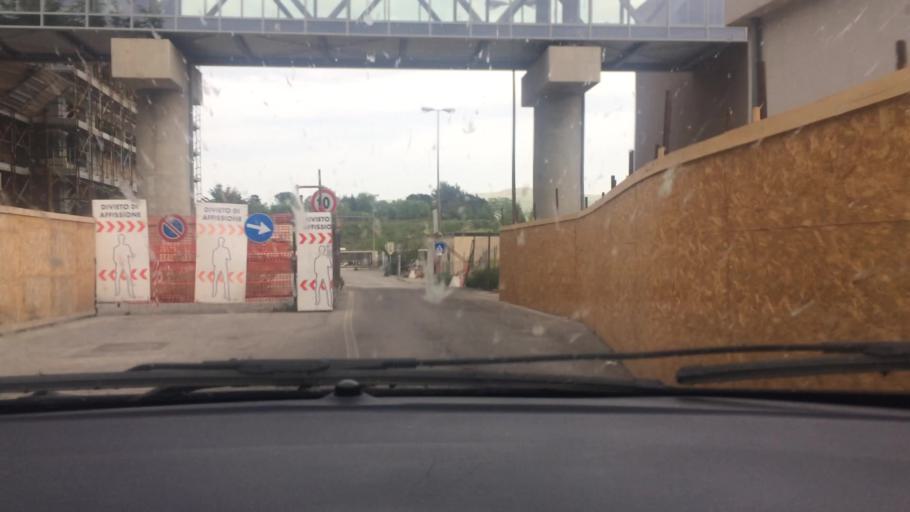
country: IT
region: Basilicate
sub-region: Provincia di Potenza
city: Potenza
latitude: 40.6510
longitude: 15.8040
